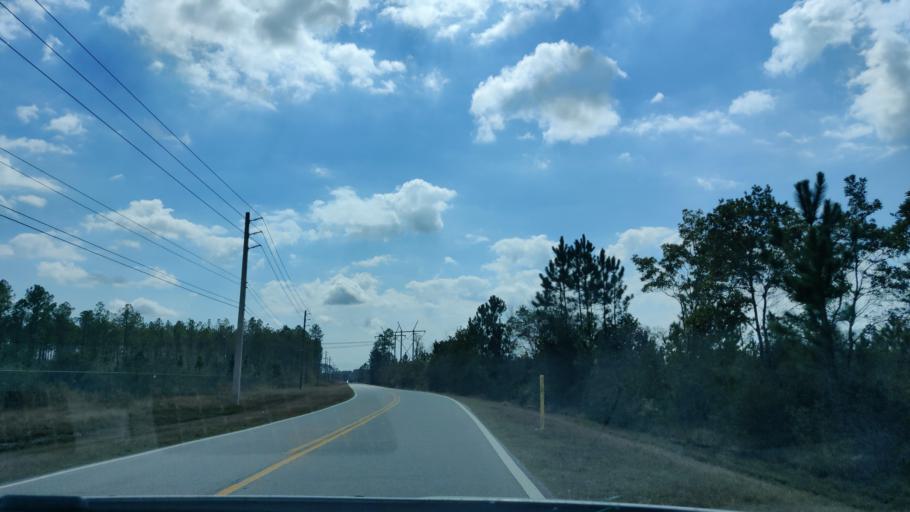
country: US
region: Florida
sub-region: Duval County
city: Baldwin
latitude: 30.2661
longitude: -81.9565
